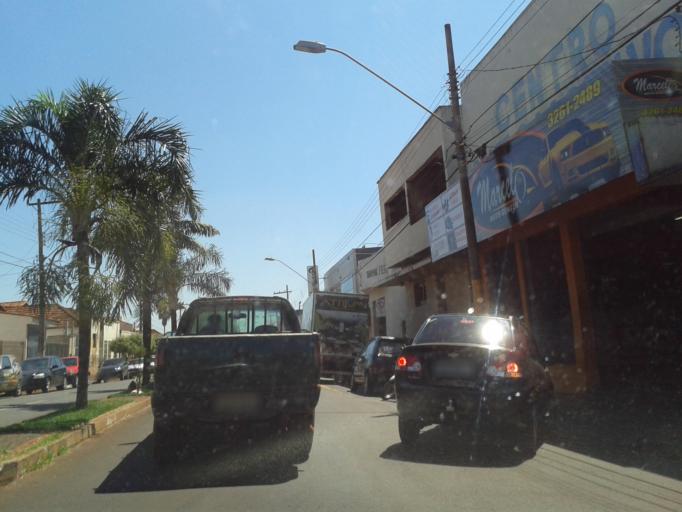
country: BR
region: Minas Gerais
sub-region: Ituiutaba
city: Ituiutaba
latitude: -18.9688
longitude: -49.4616
